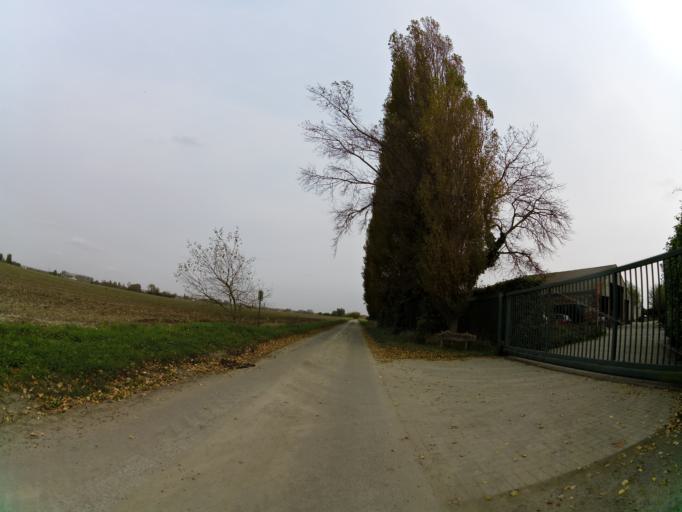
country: BE
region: Flanders
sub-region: Provincie West-Vlaanderen
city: Oudenburg
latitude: 51.2081
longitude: 3.0449
